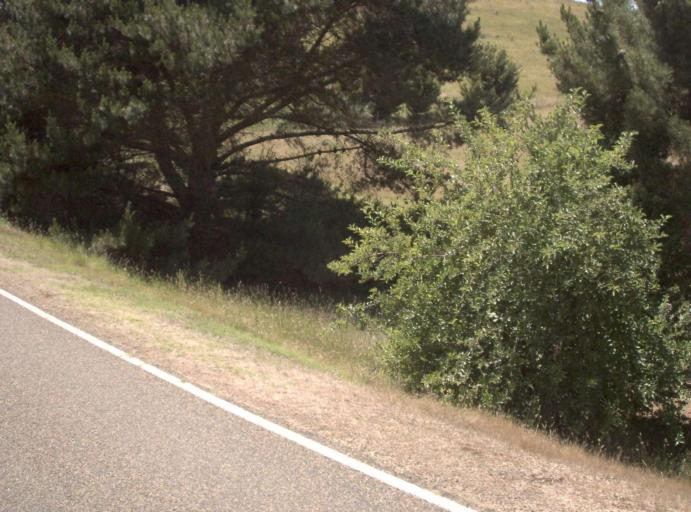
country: AU
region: Victoria
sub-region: Alpine
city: Mount Beauty
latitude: -37.1034
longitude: 147.5832
